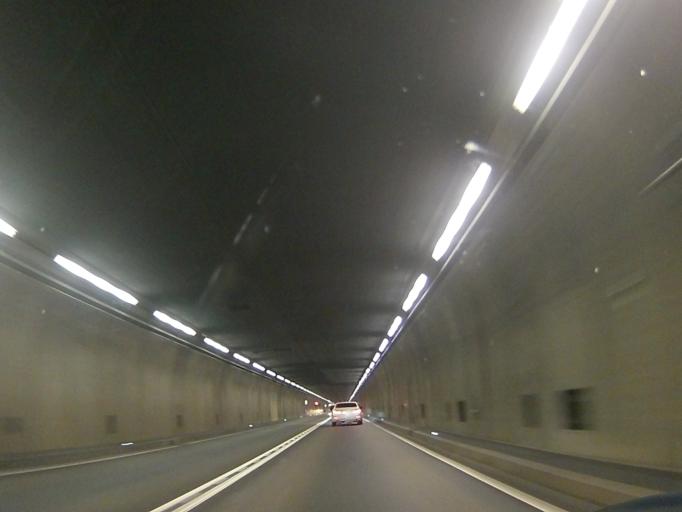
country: CH
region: Uri
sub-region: Uri
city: Andermatt
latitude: 46.6483
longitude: 8.5837
